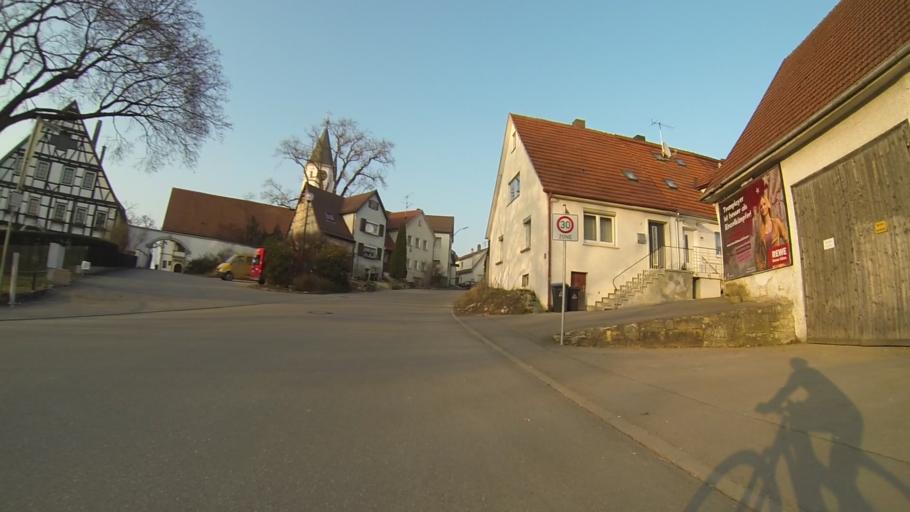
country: DE
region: Baden-Wuerttemberg
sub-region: Regierungsbezirk Stuttgart
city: Heidenheim an der Brenz
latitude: 48.7090
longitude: 10.1622
